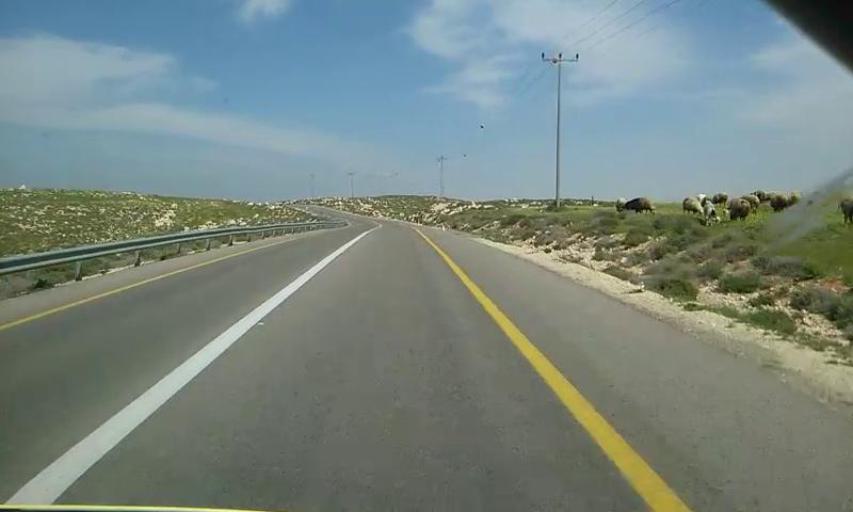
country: PS
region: West Bank
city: As Samu`
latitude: 31.3949
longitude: 35.0251
